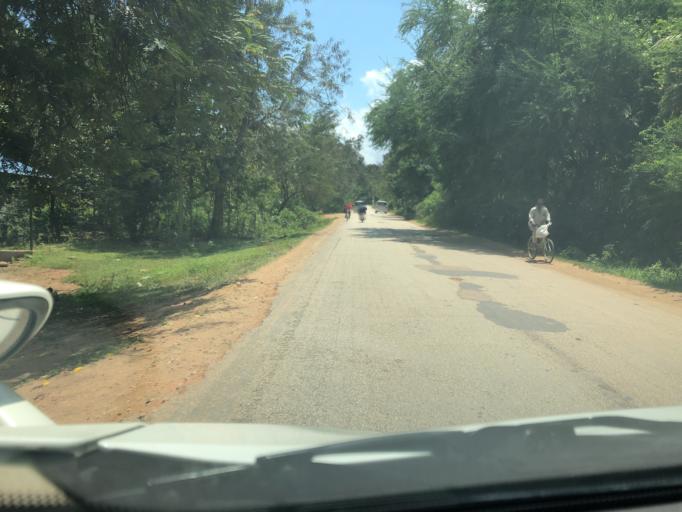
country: TZ
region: Zanzibar Central/South
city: Koani
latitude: -6.0615
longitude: 39.2520
